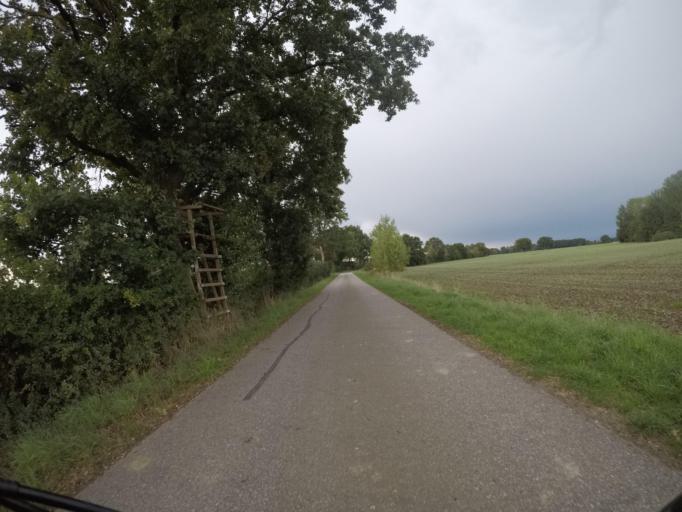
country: DE
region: Lower Saxony
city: Neu Darchau
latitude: 53.2782
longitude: 10.8812
